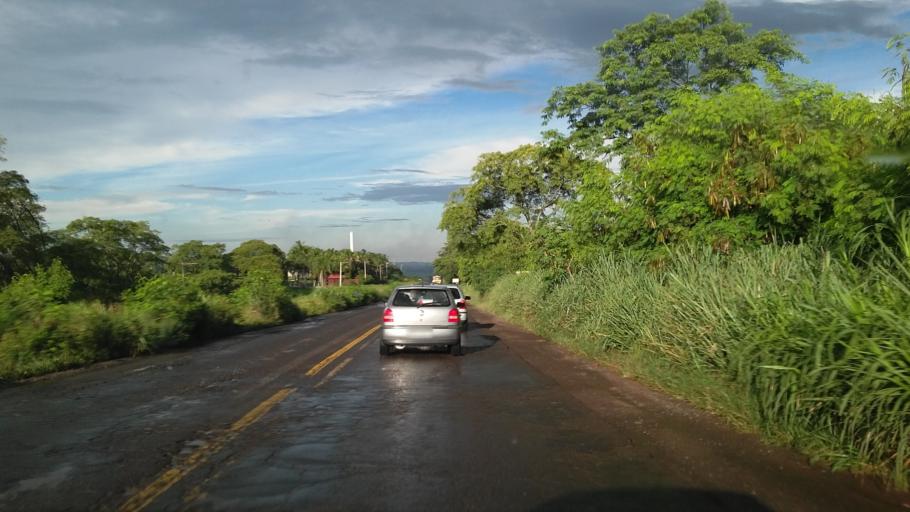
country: BR
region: Sao Paulo
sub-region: Marilia
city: Marilia
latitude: -22.1304
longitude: -49.9412
